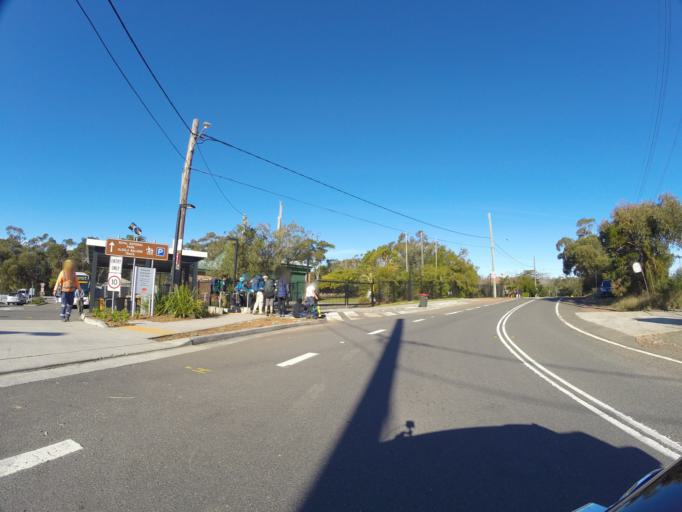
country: AU
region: New South Wales
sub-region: Wollongong
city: Helensburgh
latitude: -34.1352
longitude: 150.9949
